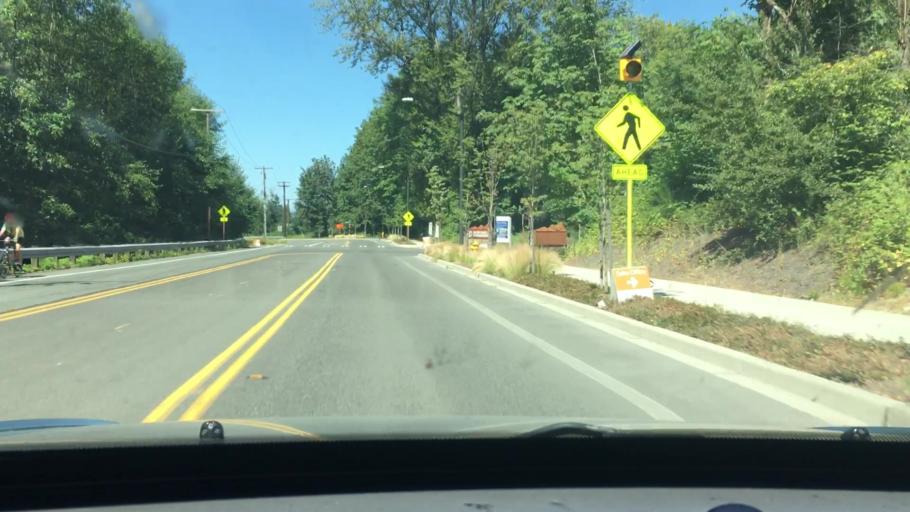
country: US
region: Washington
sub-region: King County
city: Newcastle
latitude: 47.5410
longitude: -122.1575
